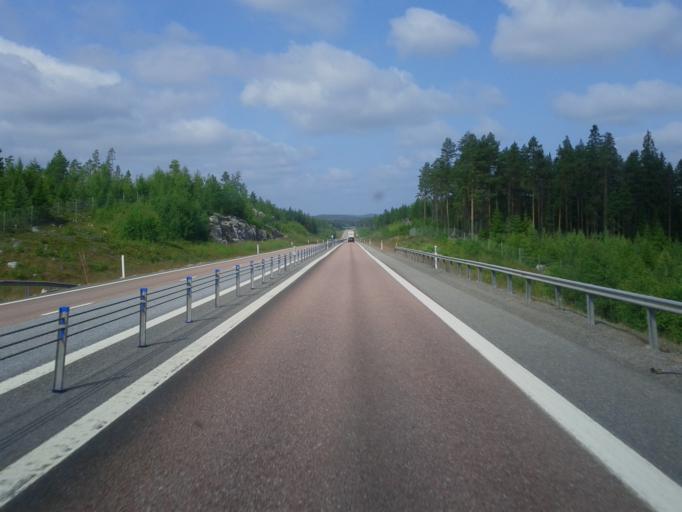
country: SE
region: Vaesterbotten
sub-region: Skelleftea Kommun
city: Soedra Bergsbyn
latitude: 64.6895
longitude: 21.0440
